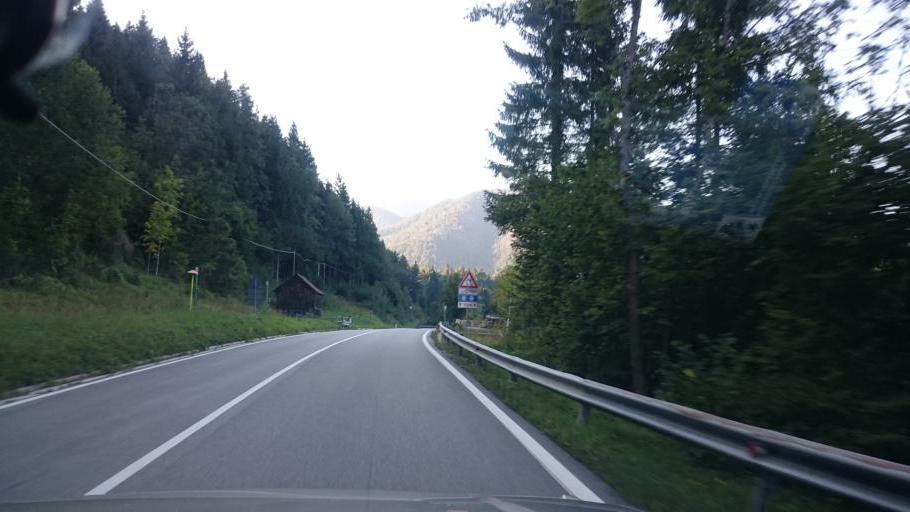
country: IT
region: Friuli Venezia Giulia
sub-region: Provincia di Udine
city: Tarvisio
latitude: 46.4914
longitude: 13.5868
